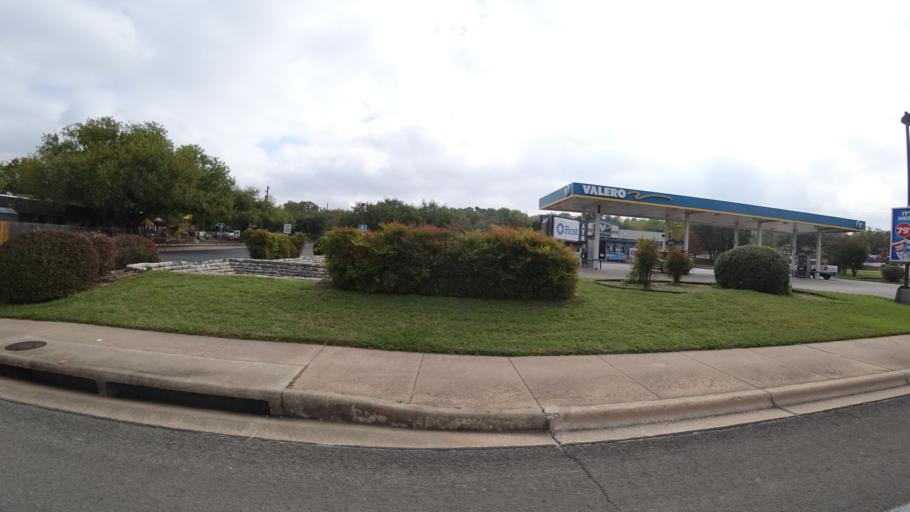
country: US
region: Texas
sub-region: Travis County
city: Shady Hollow
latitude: 30.2018
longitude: -97.8383
